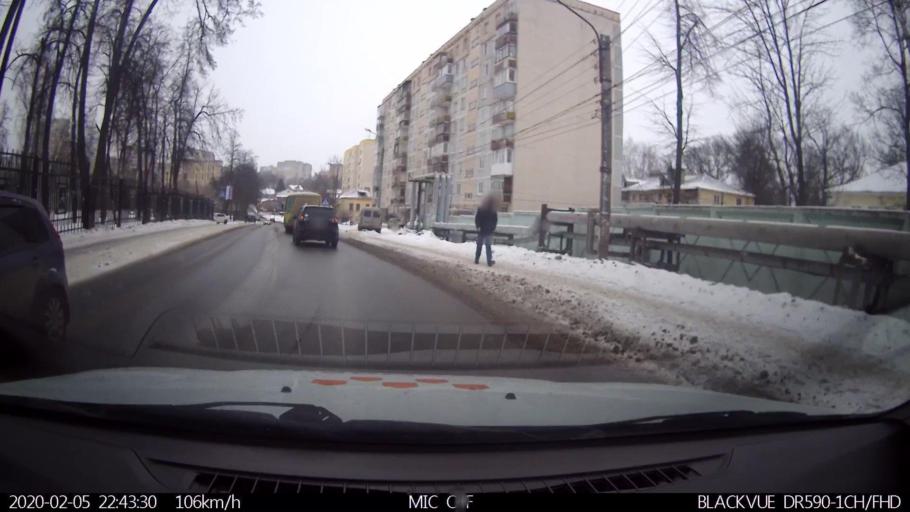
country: RU
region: Nizjnij Novgorod
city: Imeni Stepana Razina
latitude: 54.7120
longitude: 44.3788
